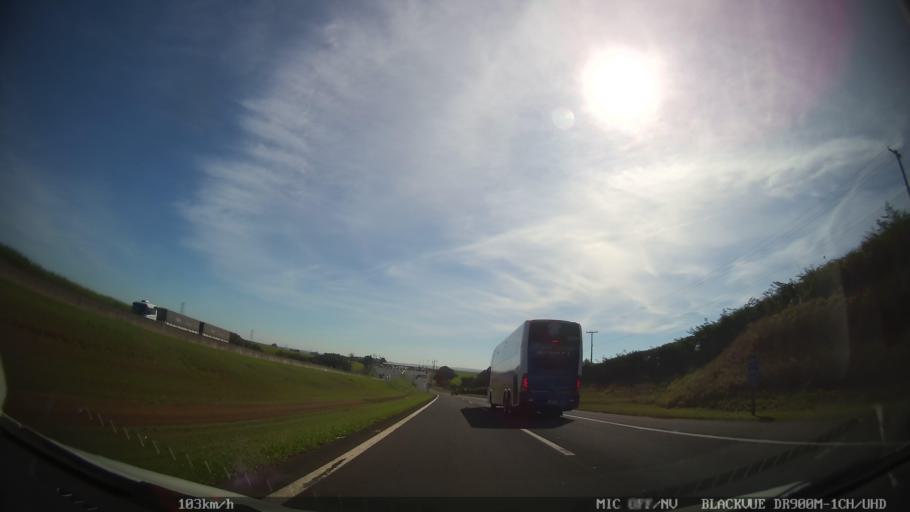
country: BR
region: Sao Paulo
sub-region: Leme
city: Leme
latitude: -22.2560
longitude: -47.3898
